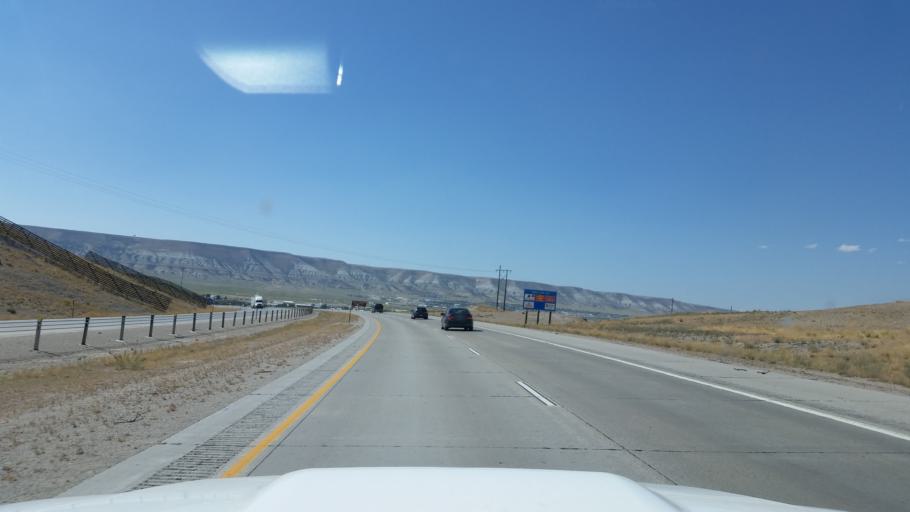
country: US
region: Wyoming
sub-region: Sweetwater County
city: Rock Springs
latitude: 41.6089
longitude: -109.2136
